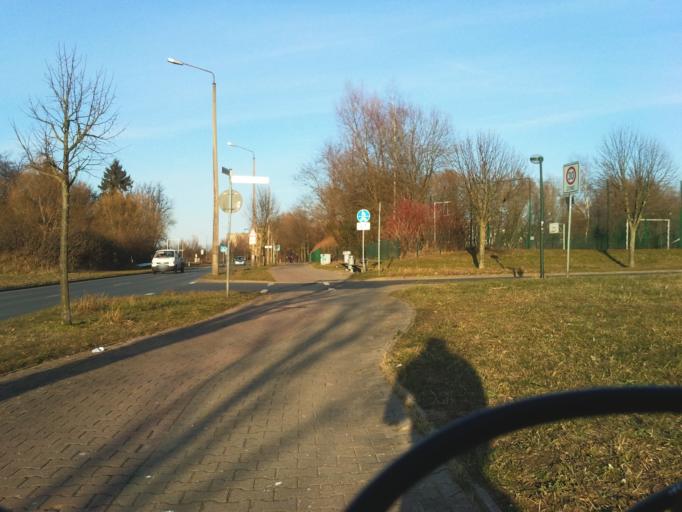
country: DE
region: Mecklenburg-Vorpommern
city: Dierkow-West
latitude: 54.1161
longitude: 12.1384
